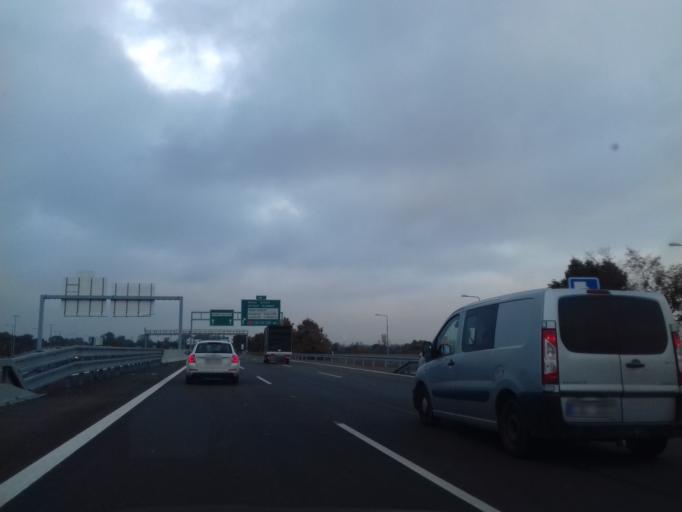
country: CZ
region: South Moravian
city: Modrice
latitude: 49.1386
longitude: 16.6357
